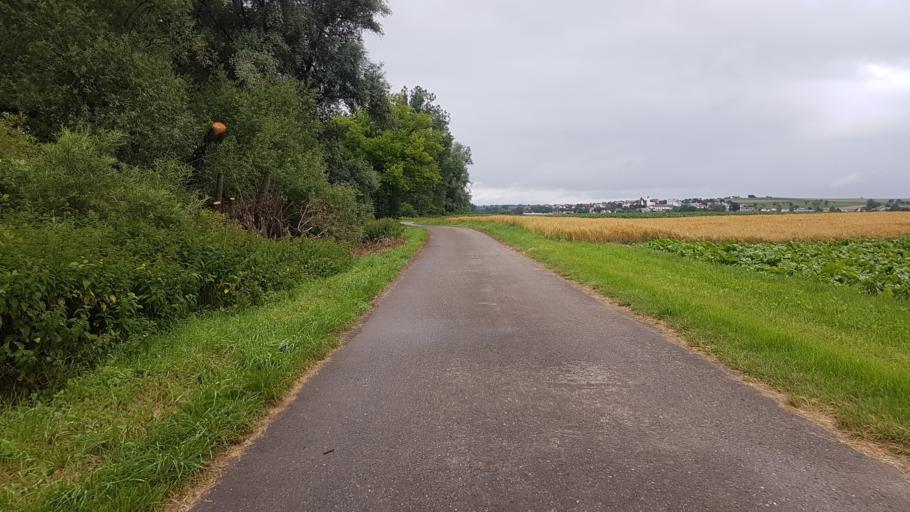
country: DE
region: Baden-Wuerttemberg
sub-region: Tuebingen Region
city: Dettingen
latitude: 48.2520
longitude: 9.7224
